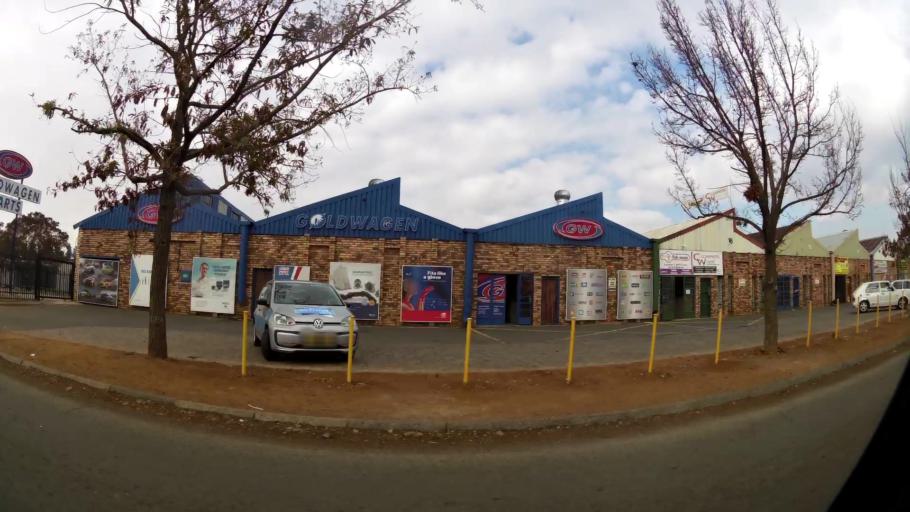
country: ZA
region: Gauteng
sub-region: Sedibeng District Municipality
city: Vanderbijlpark
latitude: -26.7042
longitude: 27.8571
